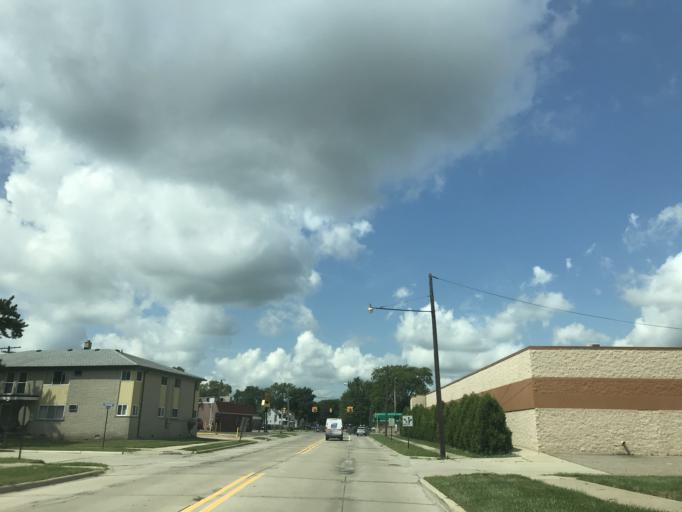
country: US
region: Michigan
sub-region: Wayne County
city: Southgate
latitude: 42.2238
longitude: -83.1926
